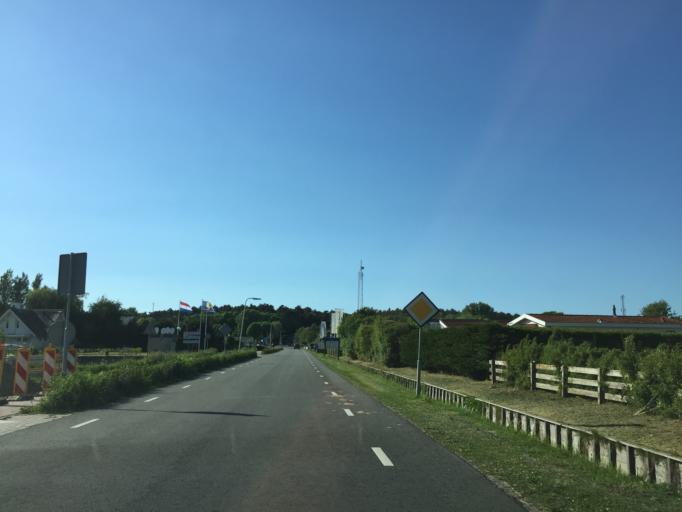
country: NL
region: South Holland
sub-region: Gemeente Noordwijkerhout
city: Noordwijkerhout
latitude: 52.2674
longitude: 4.4710
